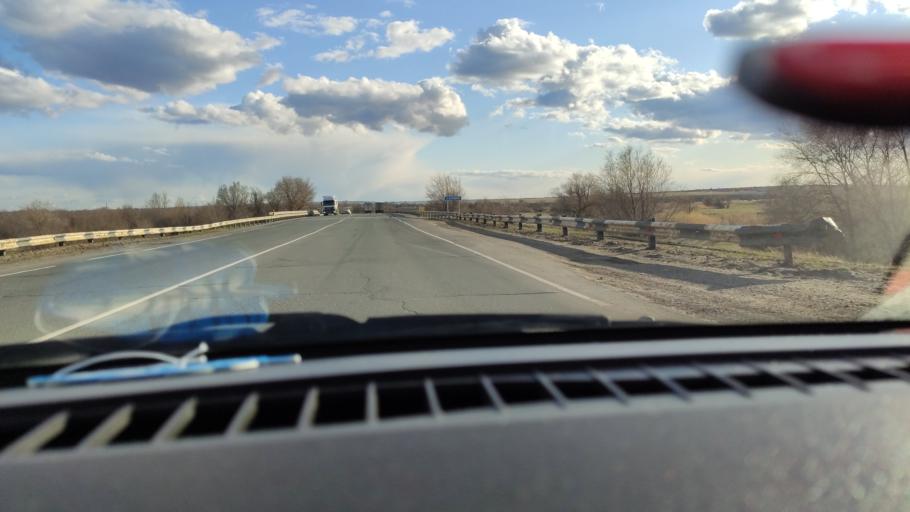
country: RU
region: Saratov
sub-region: Saratovskiy Rayon
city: Saratov
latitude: 51.7211
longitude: 46.0264
